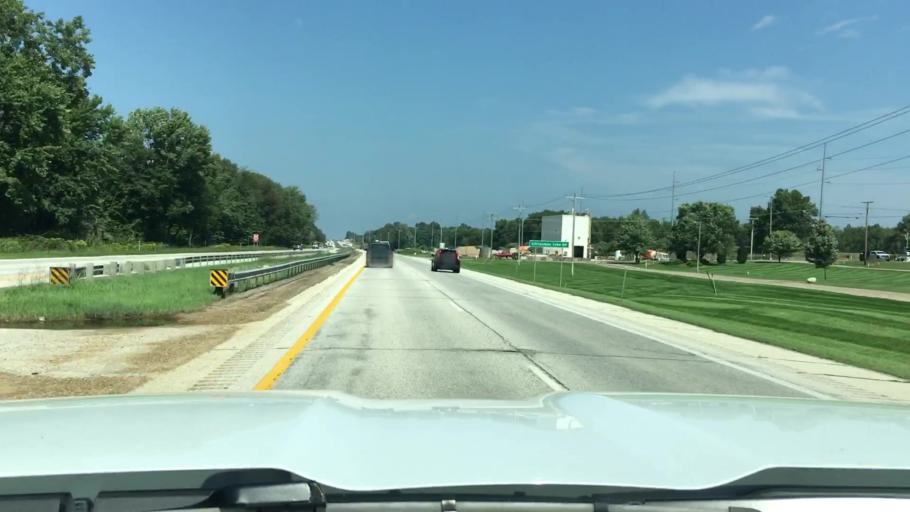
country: US
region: Michigan
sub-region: Kalamazoo County
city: Schoolcraft
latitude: 42.0479
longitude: -85.6356
